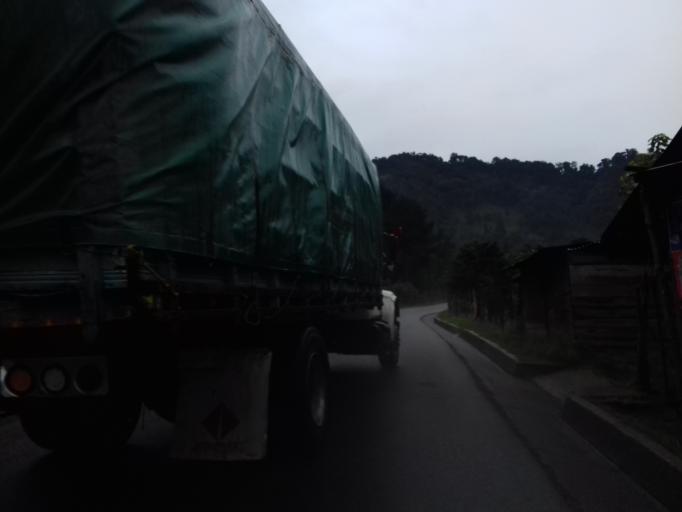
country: GT
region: Quiche
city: Nebaj
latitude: 15.3835
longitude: -91.1114
